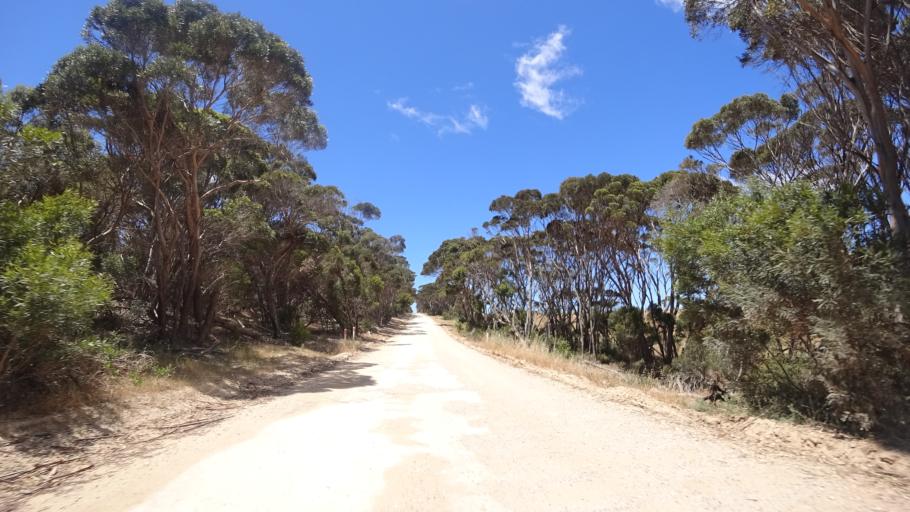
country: AU
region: South Australia
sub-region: Yankalilla
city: Normanville
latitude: -35.8180
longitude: 138.0767
